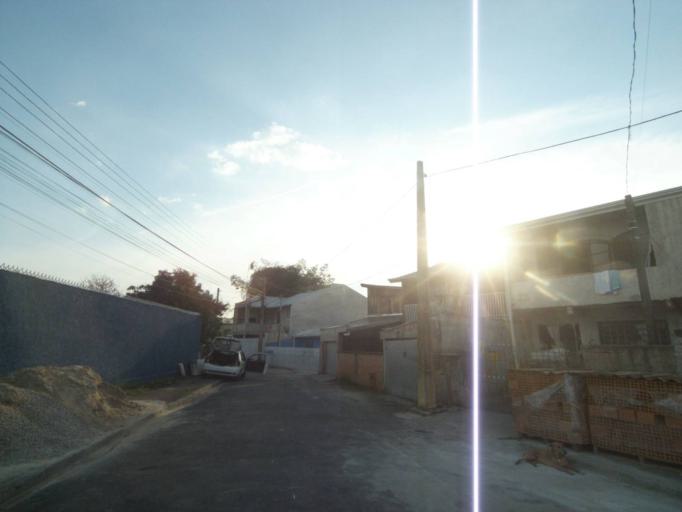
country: BR
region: Parana
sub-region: Curitiba
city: Curitiba
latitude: -25.4574
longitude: -49.3152
